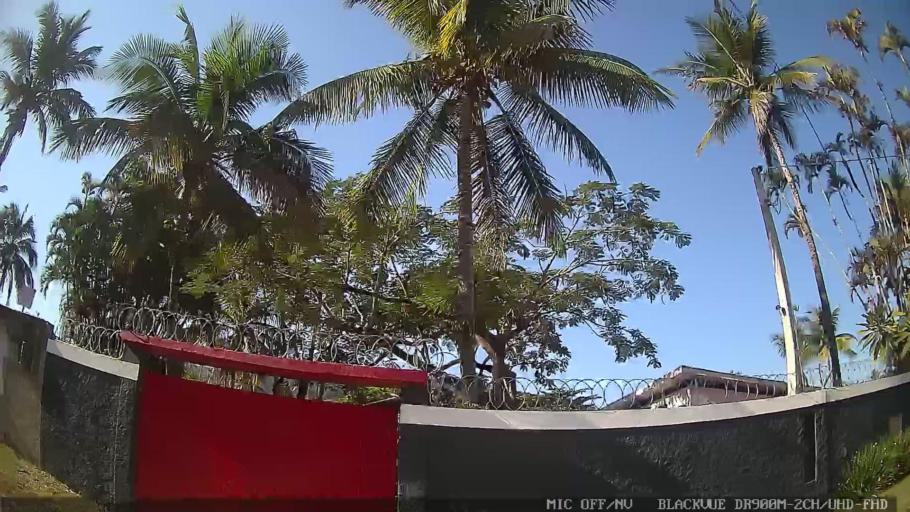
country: BR
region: Sao Paulo
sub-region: Guaruja
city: Guaruja
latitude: -24.0147
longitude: -46.2898
